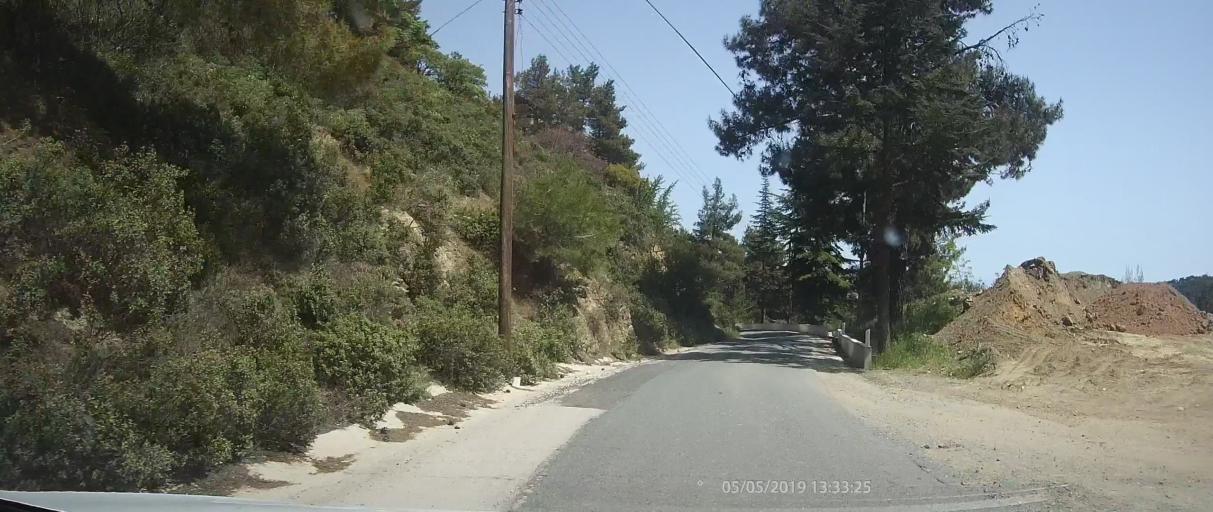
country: CY
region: Limassol
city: Pelendri
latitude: 34.8861
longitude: 32.8562
